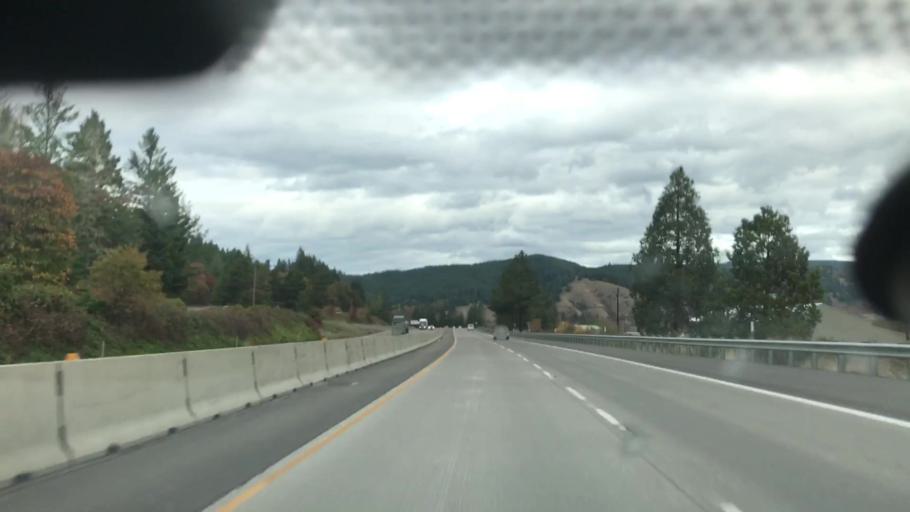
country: US
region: Oregon
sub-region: Douglas County
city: Yoncalla
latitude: 43.6079
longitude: -123.2214
